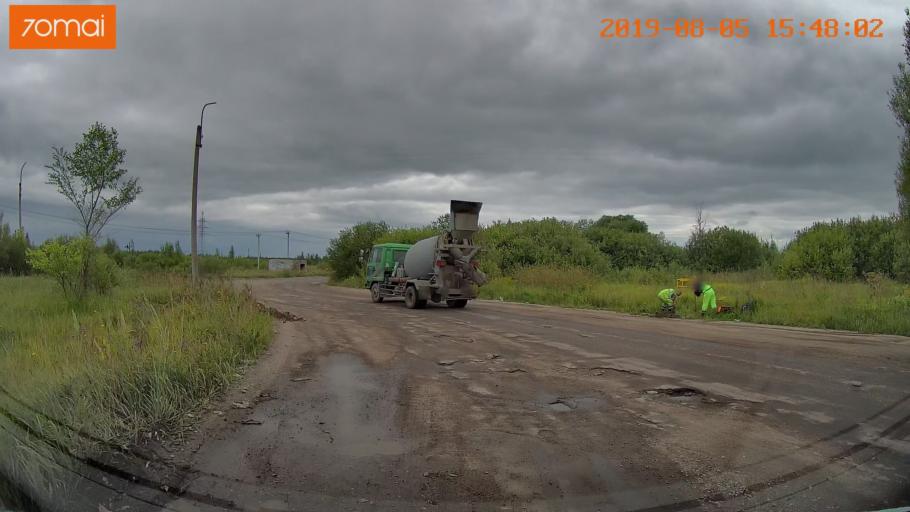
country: RU
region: Ivanovo
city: Novo-Talitsy
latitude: 56.9890
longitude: 40.9066
